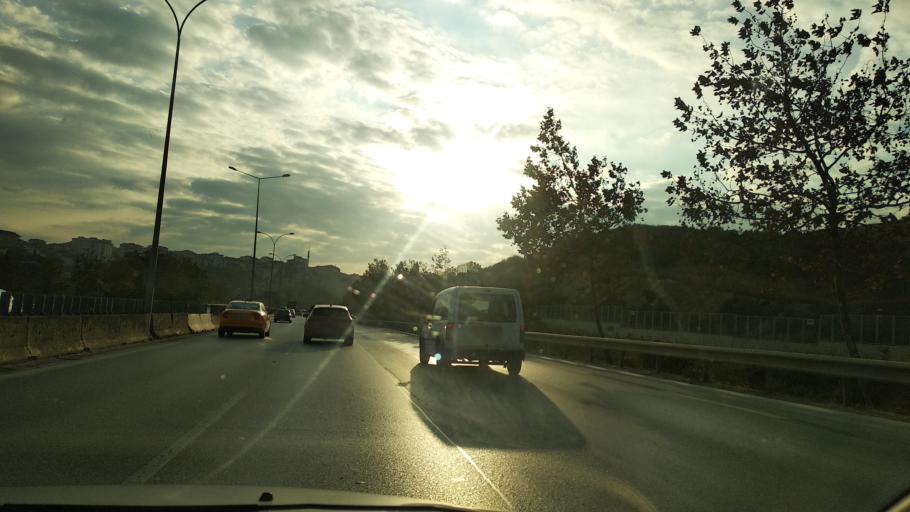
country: TR
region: Istanbul
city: Icmeler
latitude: 40.8766
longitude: 29.3036
